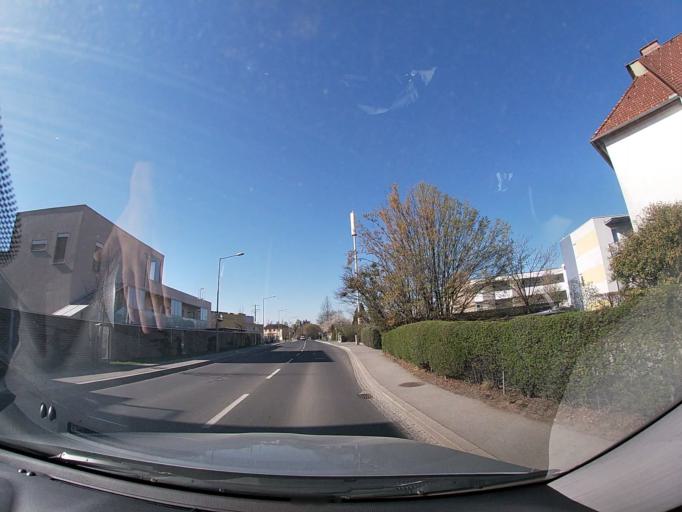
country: AT
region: Styria
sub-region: Politischer Bezirk Graz-Umgebung
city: Raaba
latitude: 47.0557
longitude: 15.4867
